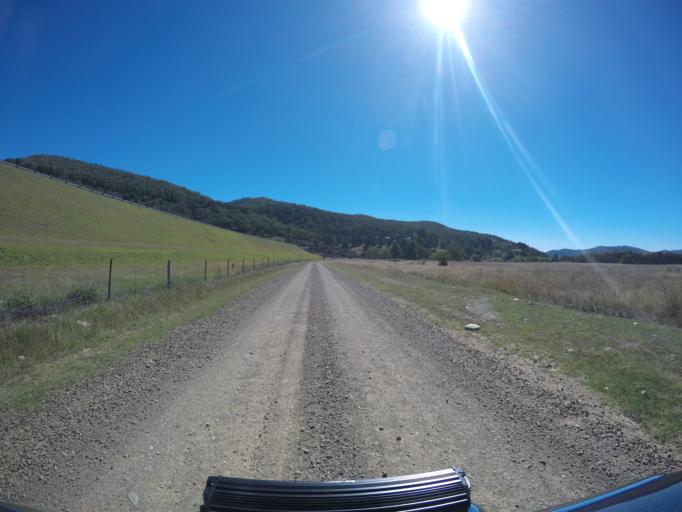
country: AU
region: New South Wales
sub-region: Snowy River
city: Jindabyne
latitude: -36.2203
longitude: 148.1132
